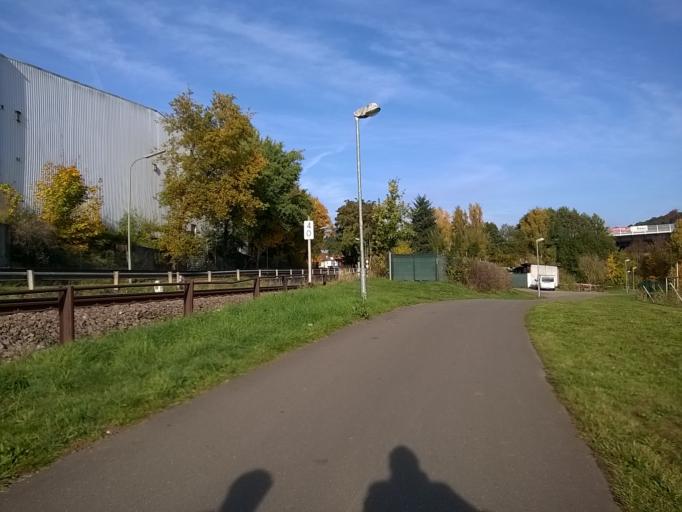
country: DE
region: Rheinland-Pfalz
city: Kaiserslautern
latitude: 49.4532
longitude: 7.7469
